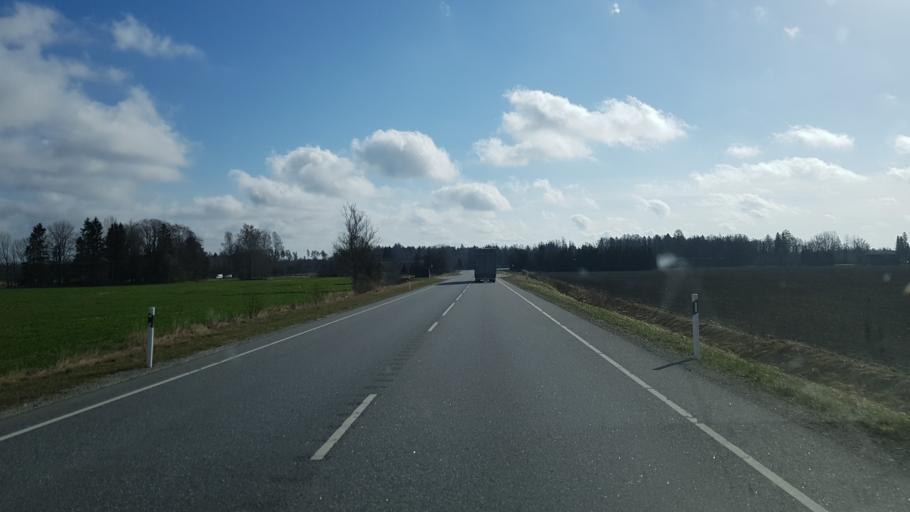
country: EE
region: Paernumaa
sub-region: Vaendra vald (alev)
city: Vandra
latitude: 58.6728
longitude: 25.1087
